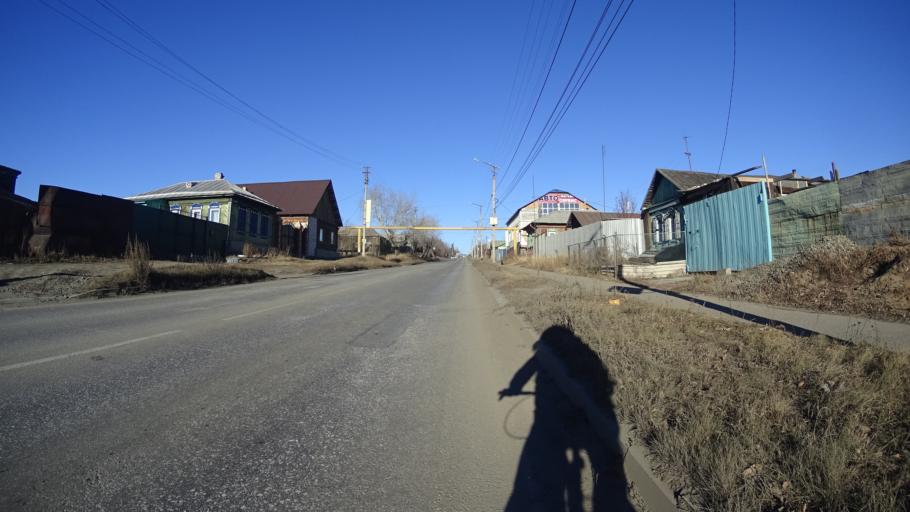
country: RU
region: Chelyabinsk
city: Troitsk
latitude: 54.0996
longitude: 61.5627
